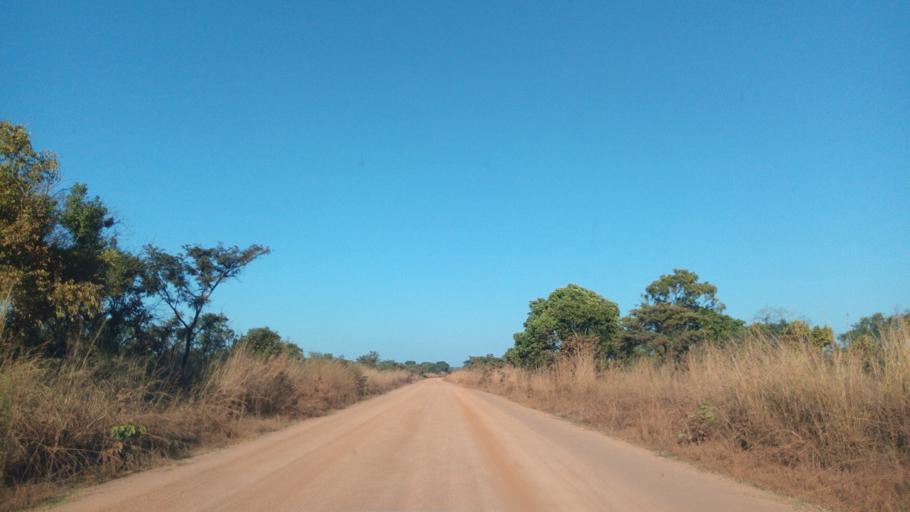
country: ZM
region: Luapula
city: Mwense
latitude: -10.5028
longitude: 28.4781
